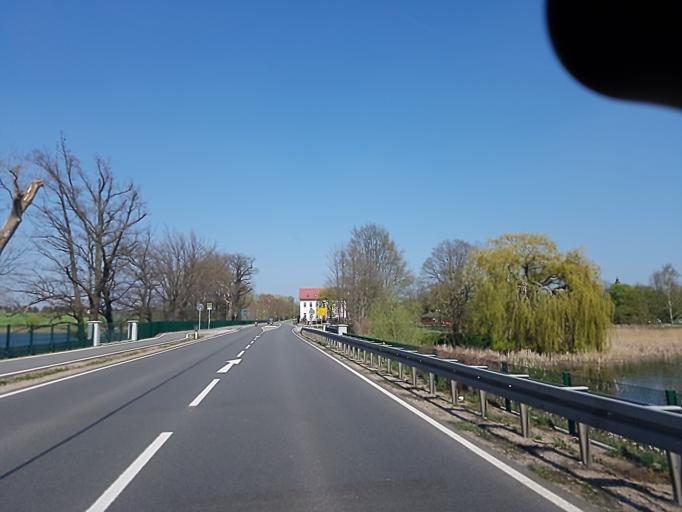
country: DE
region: Saxony
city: Wermsdorf
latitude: 51.2746
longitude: 12.9262
